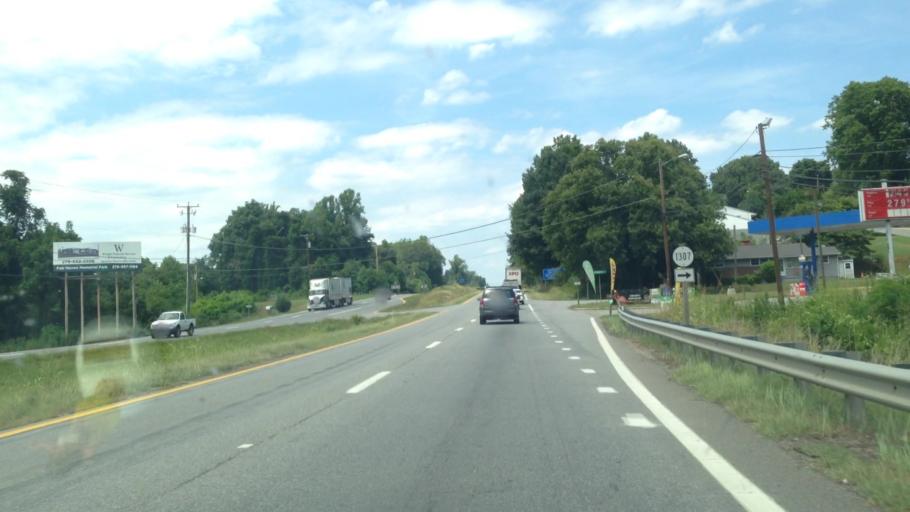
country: US
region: Virginia
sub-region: Henry County
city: Chatmoss
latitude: 36.6140
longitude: -79.8607
